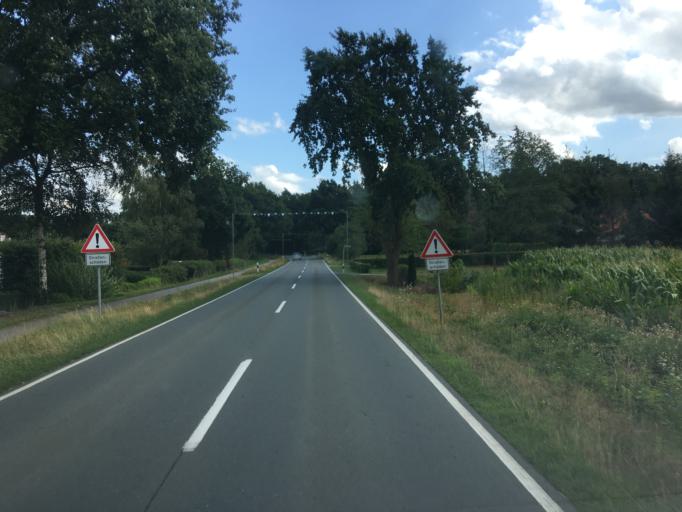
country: DE
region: Lower Saxony
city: Friesoythe
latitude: 53.0801
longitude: 7.8376
